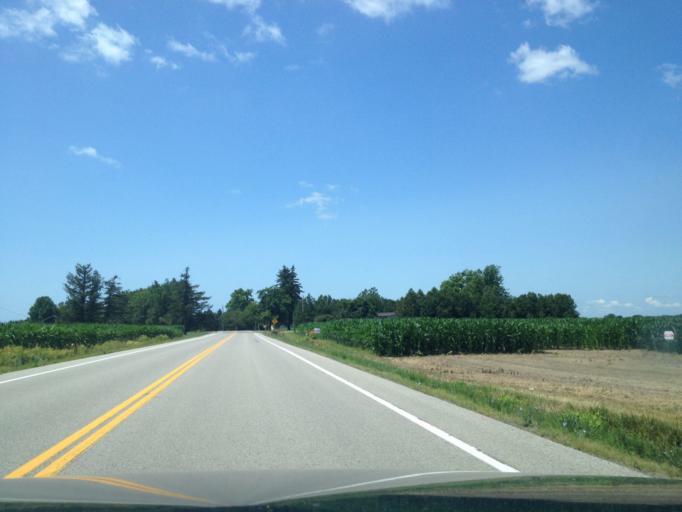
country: CA
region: Ontario
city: Norfolk County
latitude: 42.5929
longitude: -80.4973
